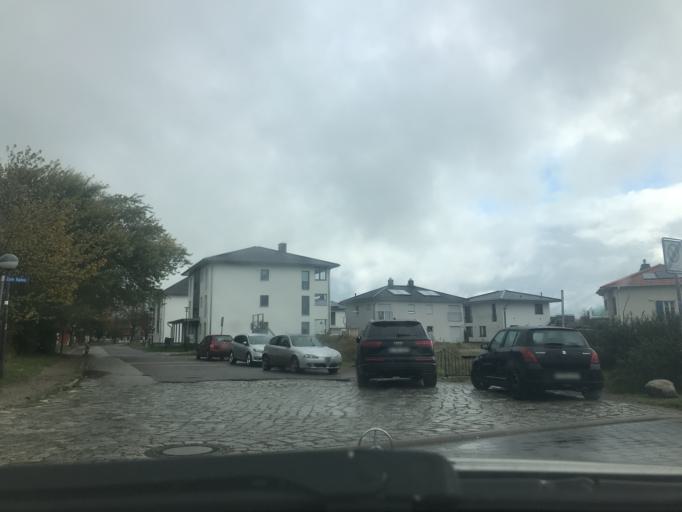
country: DE
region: Mecklenburg-Vorpommern
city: Kroslin
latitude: 54.1351
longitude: 13.7674
